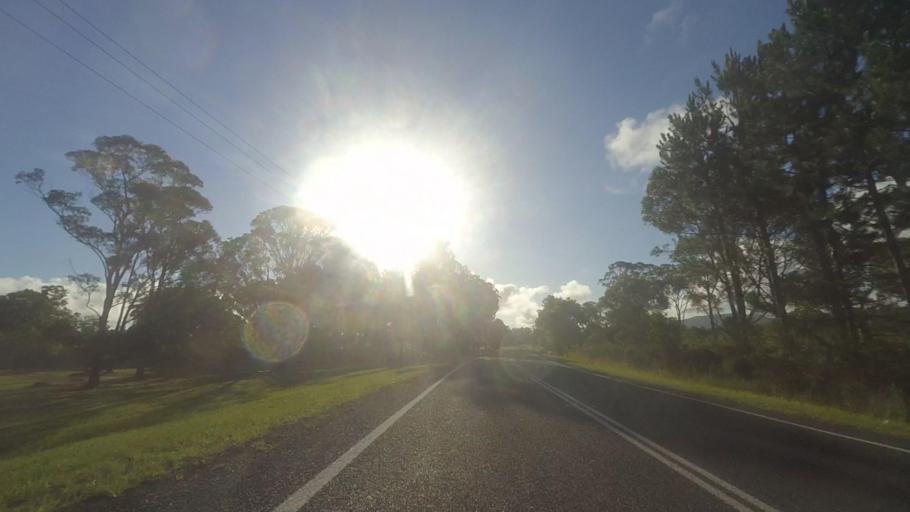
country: AU
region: New South Wales
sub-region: Great Lakes
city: Nabiac
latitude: -32.0925
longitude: 152.4531
